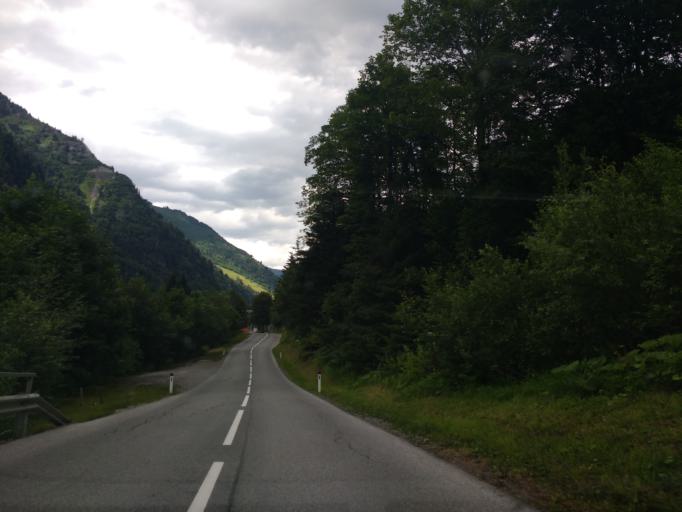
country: AT
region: Salzburg
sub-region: Politischer Bezirk Zell am See
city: Kaprun
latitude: 47.2267
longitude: 12.7266
